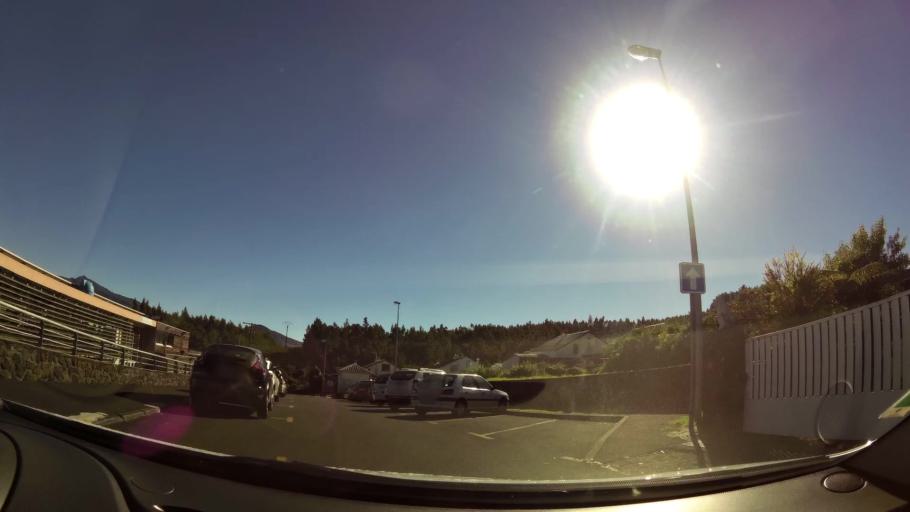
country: RE
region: Reunion
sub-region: Reunion
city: Le Tampon
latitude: -21.2210
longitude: 55.5574
